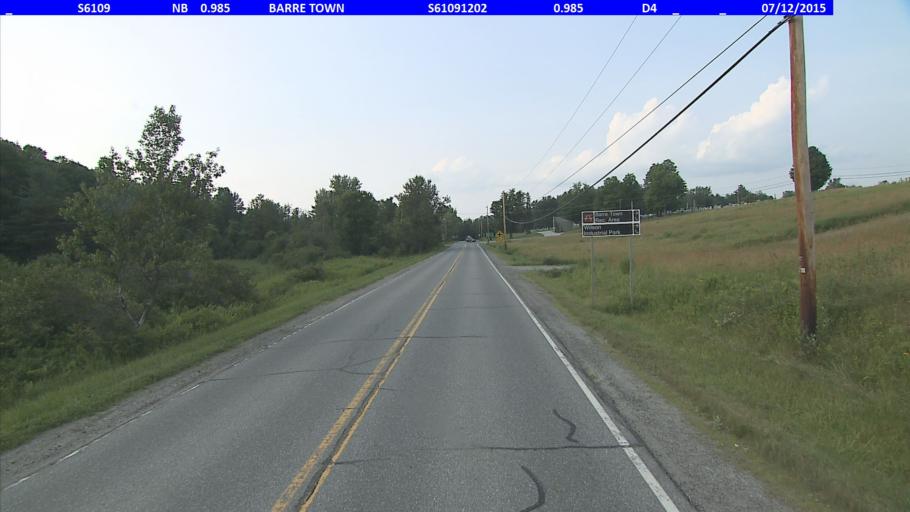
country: US
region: Vermont
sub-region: Washington County
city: South Barre
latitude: 44.1685
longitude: -72.4922
